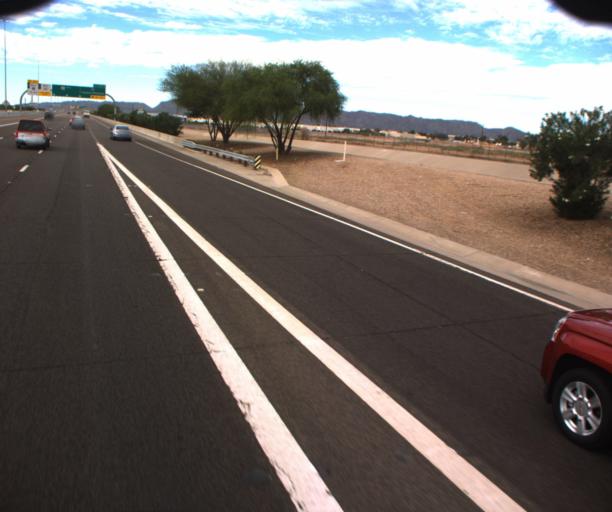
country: US
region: Arizona
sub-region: Maricopa County
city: Guadalupe
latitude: 33.2932
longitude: -111.9503
